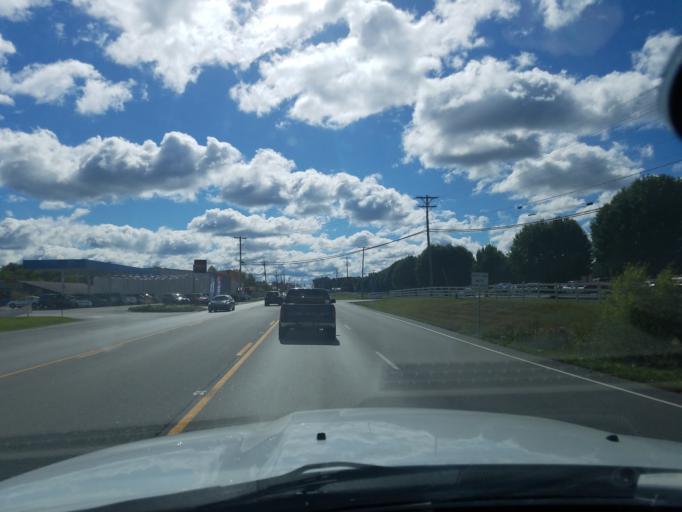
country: US
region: Kentucky
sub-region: Laurel County
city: London
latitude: 37.1060
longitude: -84.0716
